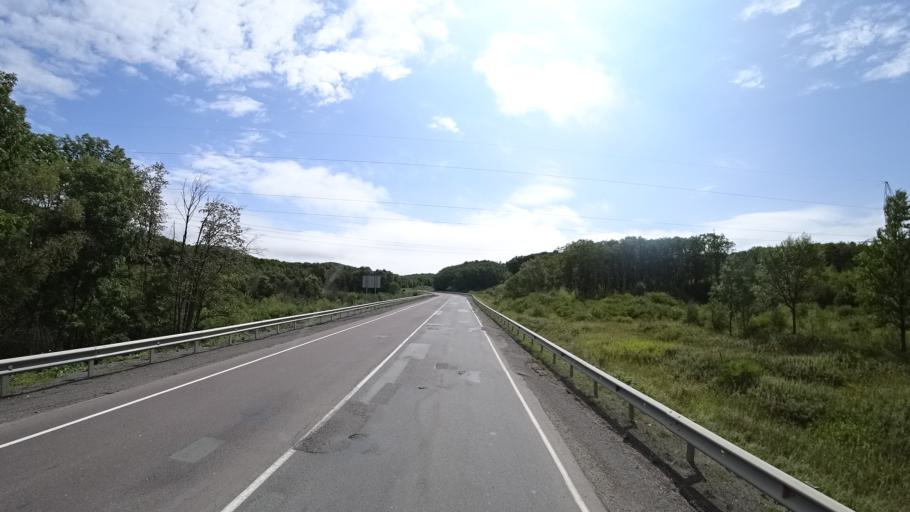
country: RU
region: Primorskiy
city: Lyalichi
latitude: 44.1350
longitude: 132.4277
